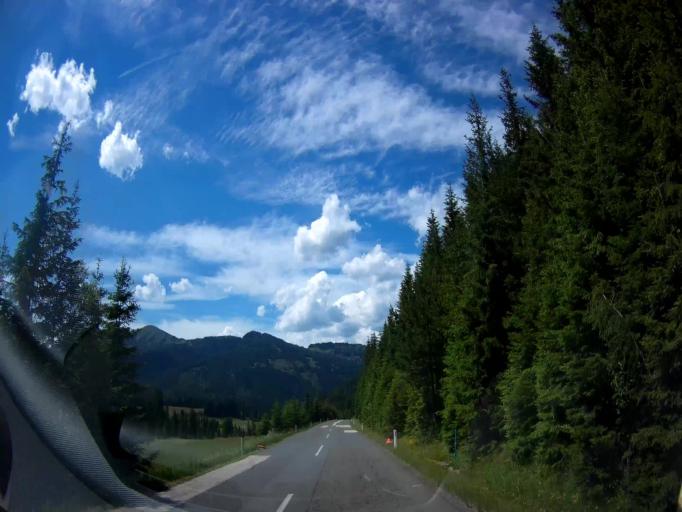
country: AT
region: Styria
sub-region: Politischer Bezirk Murau
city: Stadl an der Mur
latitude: 46.9649
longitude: 14.0211
